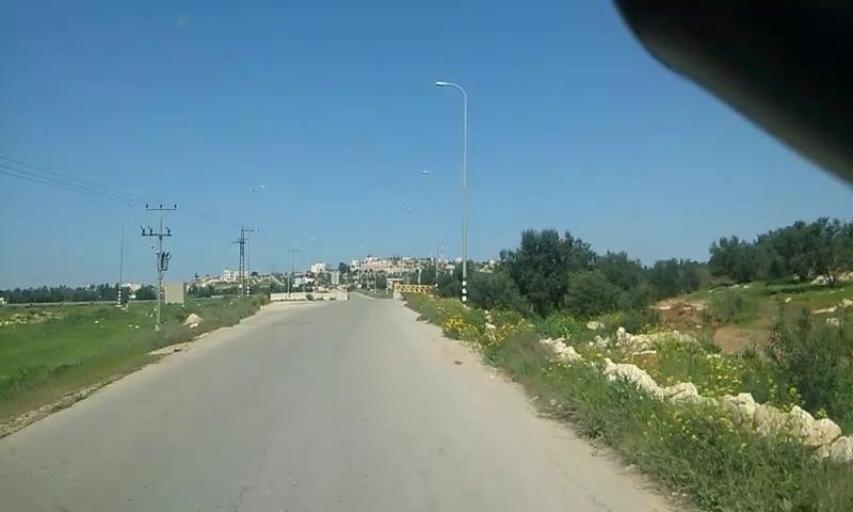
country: PS
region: West Bank
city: Bayt `Awwa
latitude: 31.4971
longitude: 34.9613
